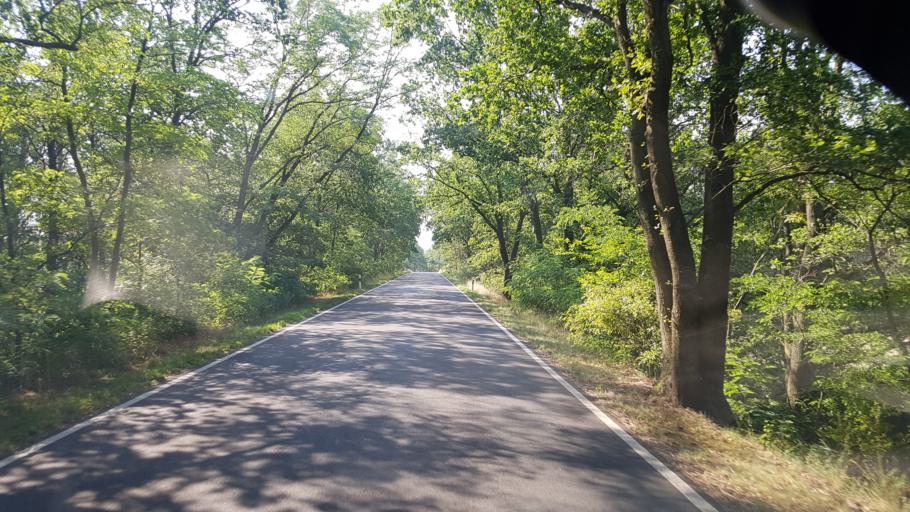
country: DE
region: Brandenburg
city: Cottbus
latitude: 51.7085
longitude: 14.4256
